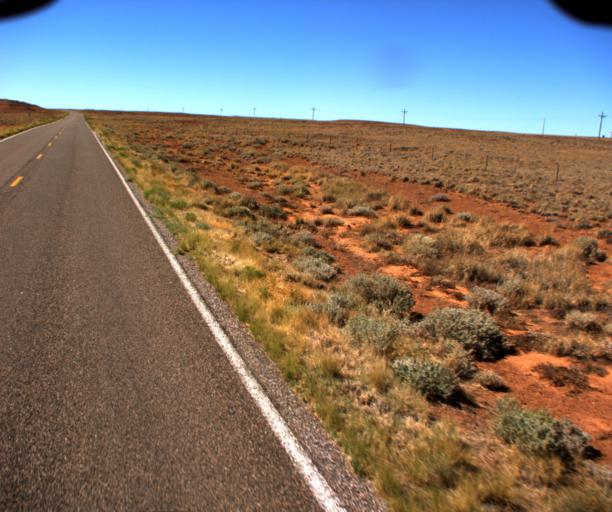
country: US
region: Arizona
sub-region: Coconino County
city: LeChee
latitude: 35.2065
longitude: -110.9485
